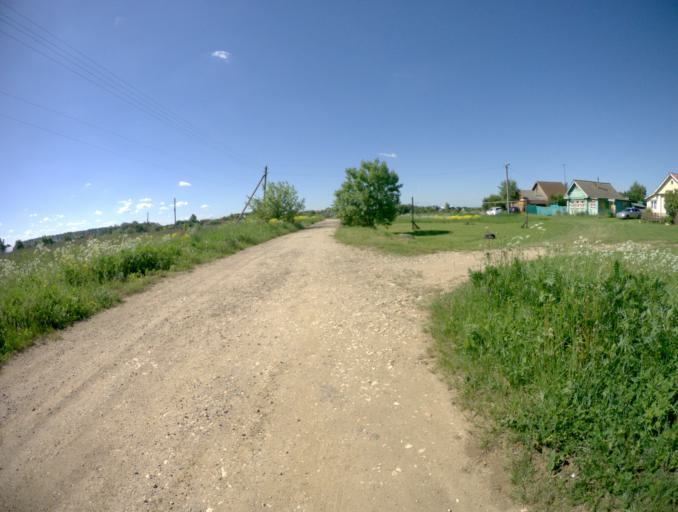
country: RU
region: Ivanovo
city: Gavrilov Posad
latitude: 56.5193
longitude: 40.2134
